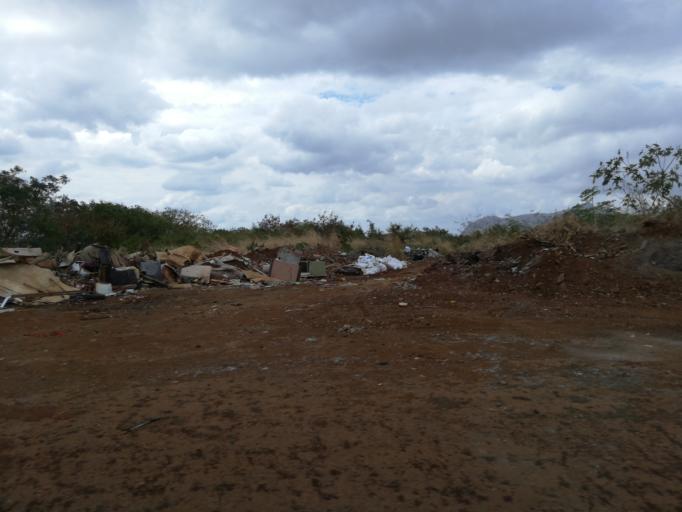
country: MU
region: Black River
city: Petite Riviere
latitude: -20.2068
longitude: 57.4582
